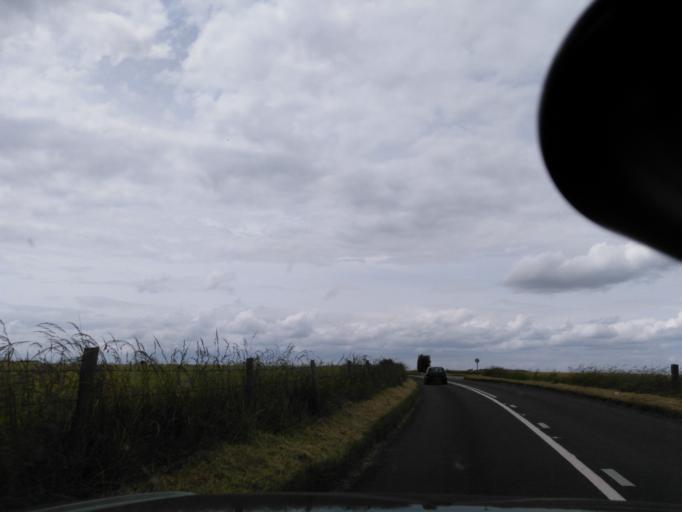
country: GB
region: England
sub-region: Wiltshire
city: Shrewton
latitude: 51.2020
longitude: -1.9214
